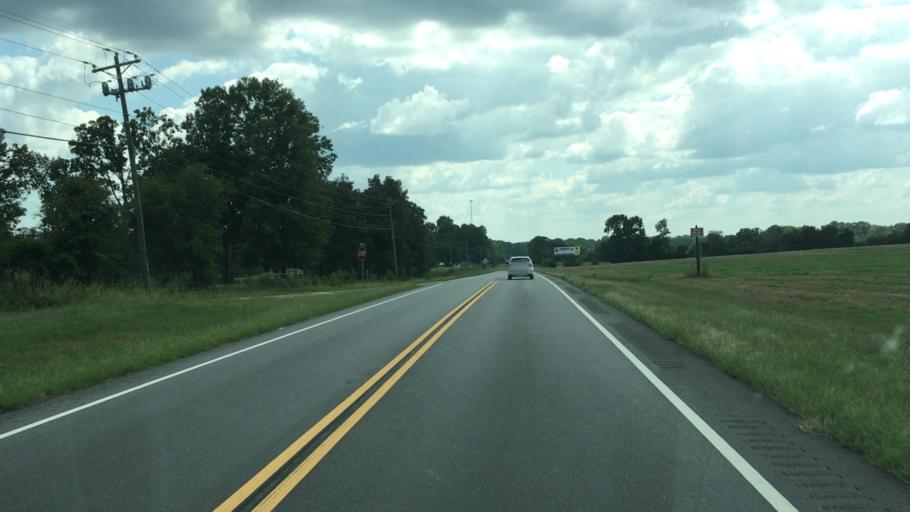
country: US
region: Georgia
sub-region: Putnam County
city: Eatonton
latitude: 33.3917
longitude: -83.3708
